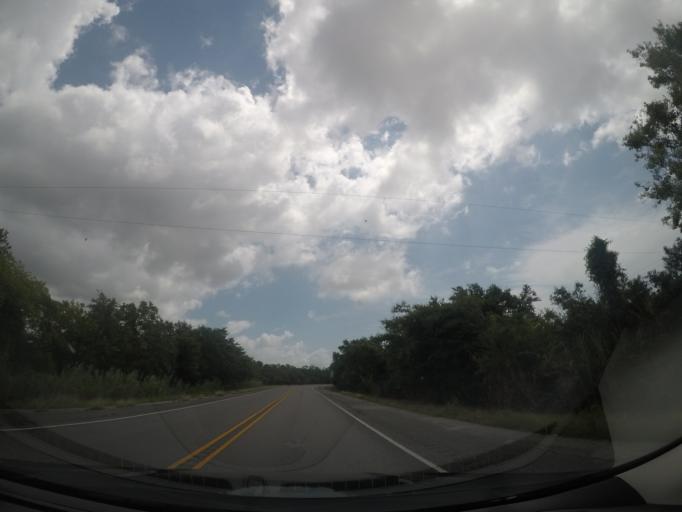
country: US
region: Louisiana
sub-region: Saint Tammany Parish
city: Eden Isle
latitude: 30.0897
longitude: -89.7841
